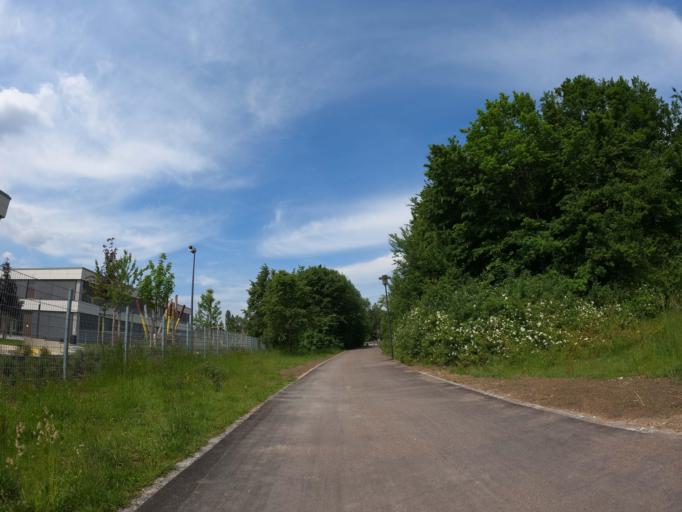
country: DE
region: Bavaria
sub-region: Upper Bavaria
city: Unterfoehring
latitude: 48.1869
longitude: 11.6466
